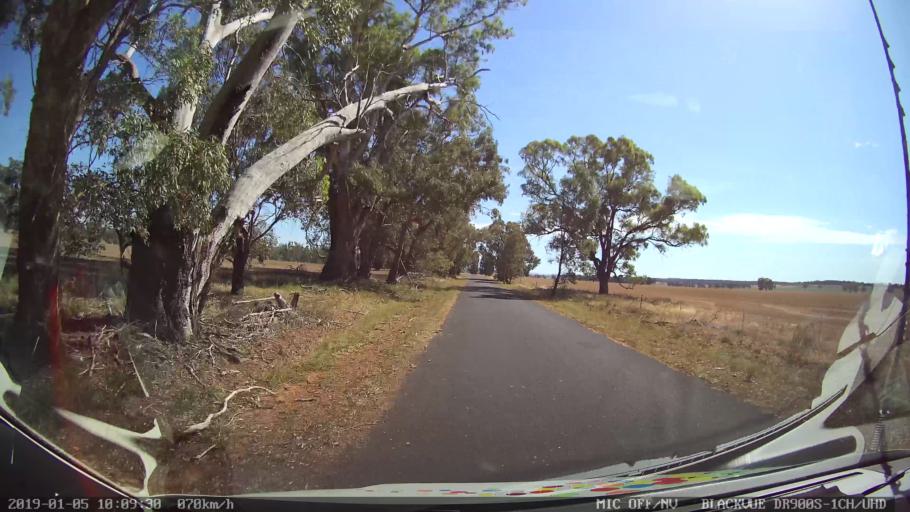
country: AU
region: New South Wales
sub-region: Gilgandra
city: Gilgandra
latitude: -31.6309
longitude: 148.8872
